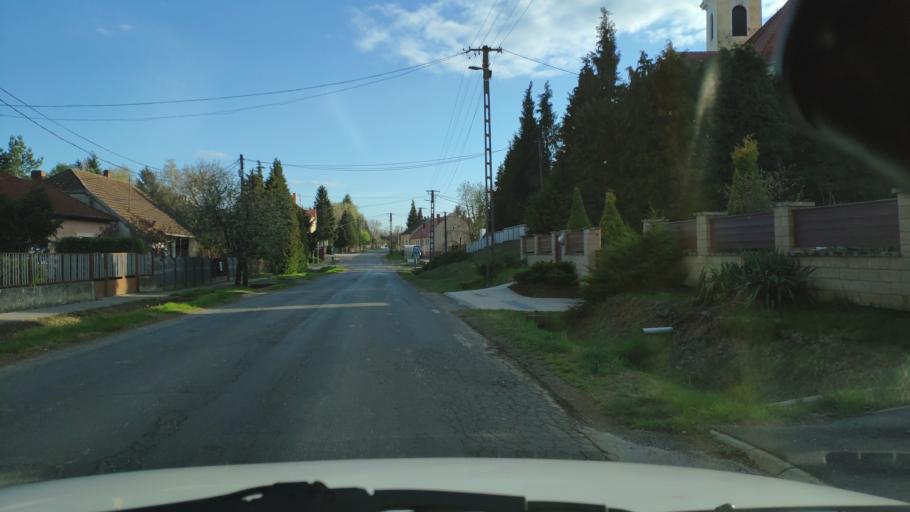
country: HU
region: Zala
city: Zalakomar
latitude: 46.4535
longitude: 17.1253
